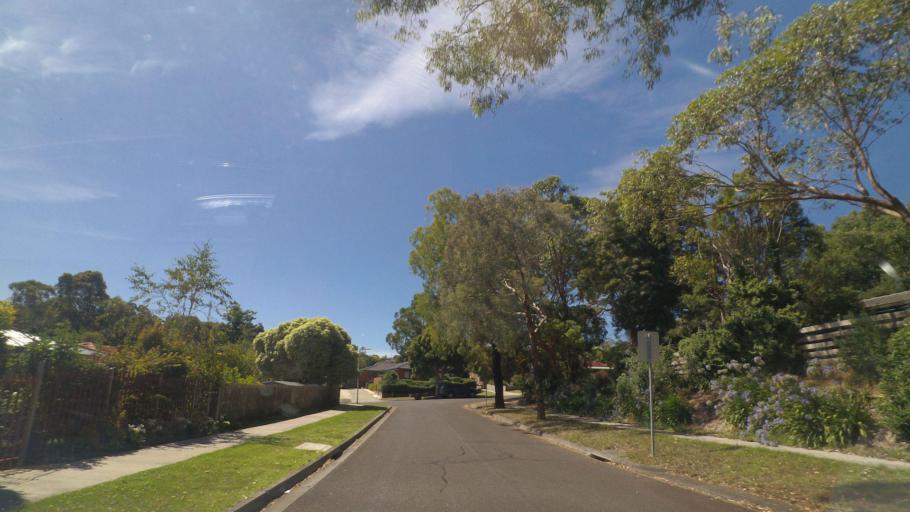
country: AU
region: Victoria
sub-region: Yarra Ranges
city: Lilydale
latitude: -37.7657
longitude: 145.3292
